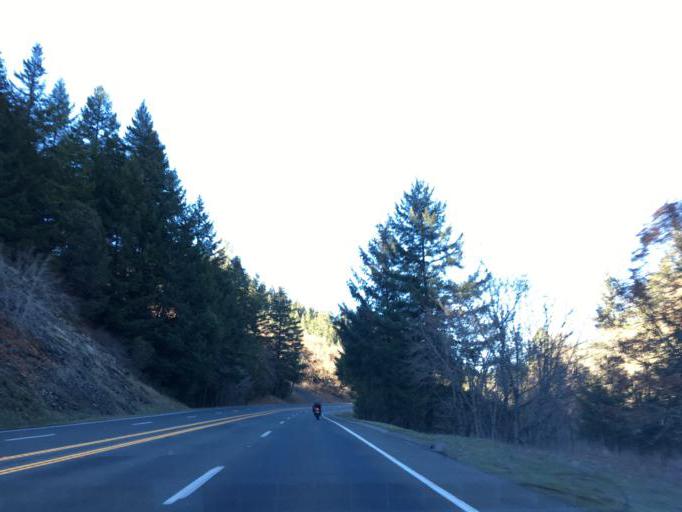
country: US
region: California
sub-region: Mendocino County
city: Laytonville
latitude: 39.5925
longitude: -123.4534
